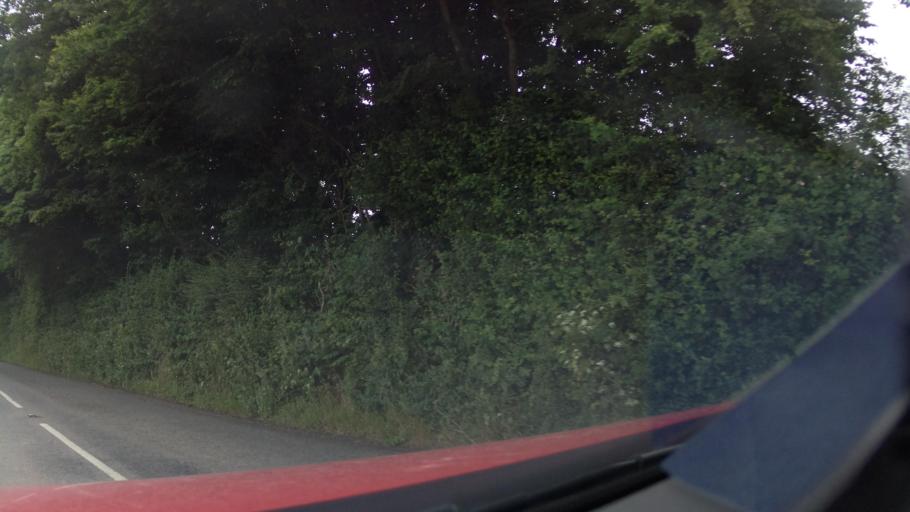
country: GB
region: England
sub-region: Devon
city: Chudleigh
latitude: 50.6686
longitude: -3.6466
